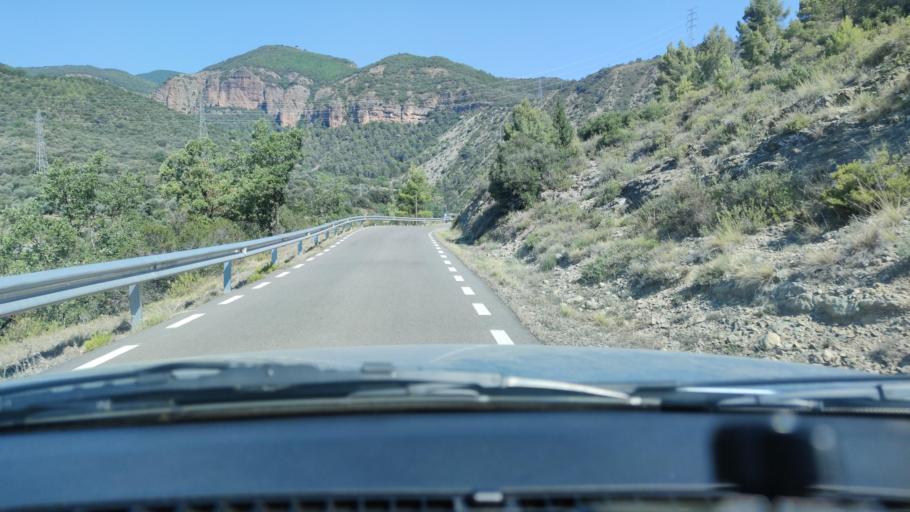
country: ES
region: Catalonia
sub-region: Provincia de Lleida
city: Senterada
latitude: 42.2837
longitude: 0.9390
